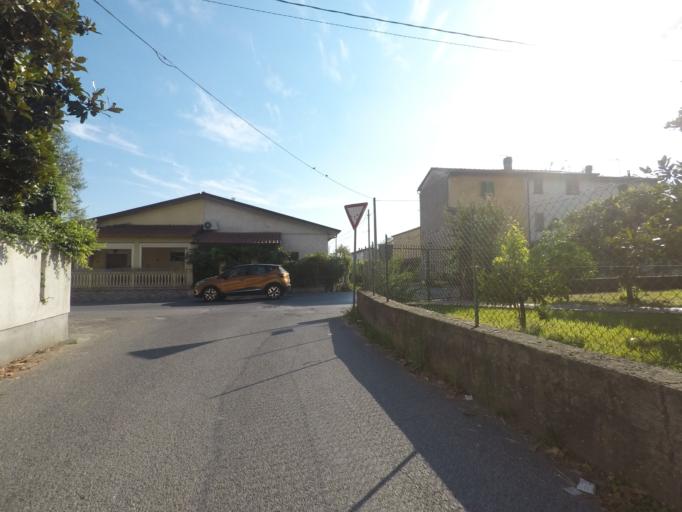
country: IT
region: Tuscany
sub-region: Provincia di Massa-Carrara
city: Massa
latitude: 44.0142
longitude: 10.1395
